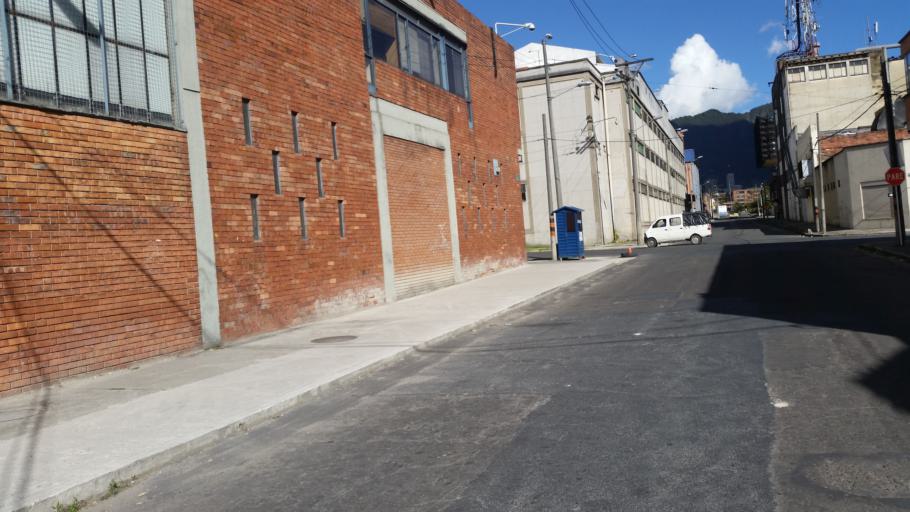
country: CO
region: Bogota D.C.
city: Bogota
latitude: 4.6212
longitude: -74.0923
